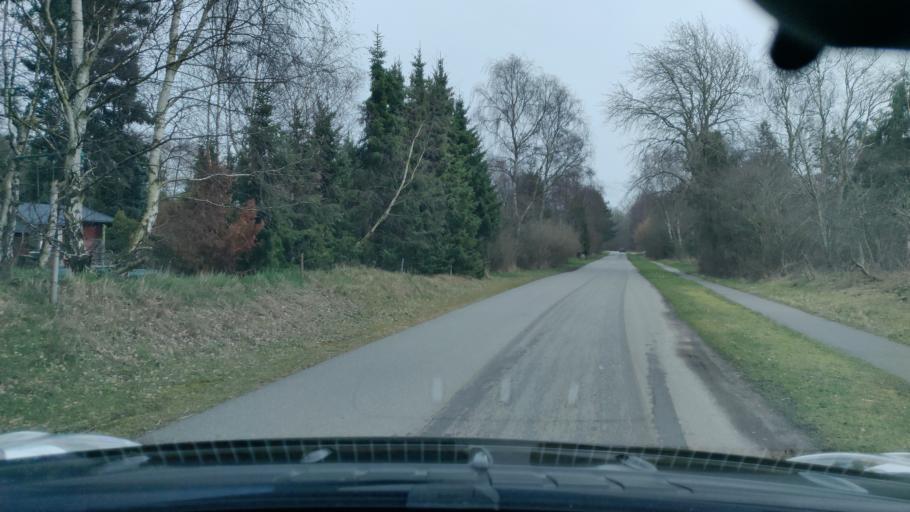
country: DK
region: Zealand
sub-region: Odsherred Kommune
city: Hojby
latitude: 55.8954
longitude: 11.5376
